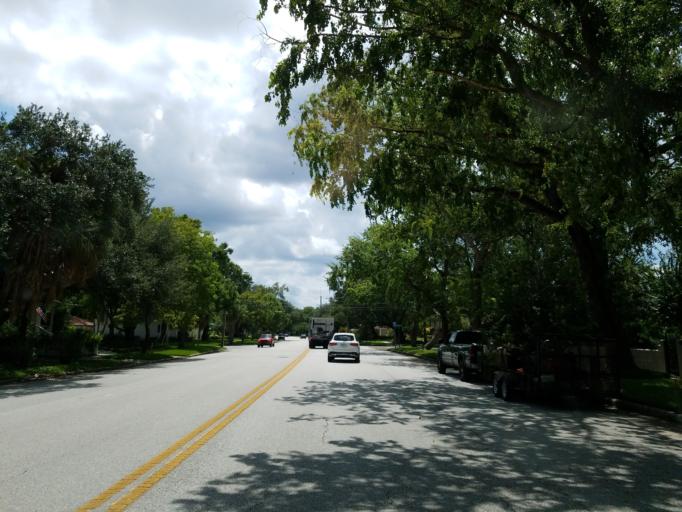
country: US
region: Florida
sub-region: Hillsborough County
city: Tampa
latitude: 27.9251
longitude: -82.4585
